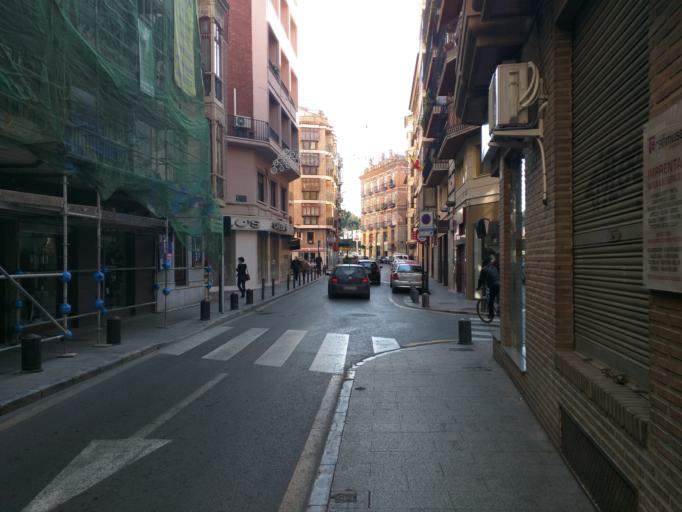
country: ES
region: Murcia
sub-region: Murcia
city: Murcia
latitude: 37.9841
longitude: -1.1332
